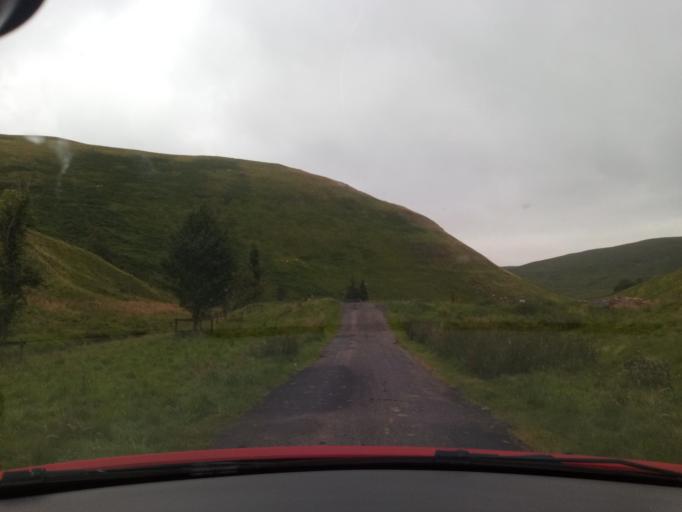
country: GB
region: England
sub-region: Northumberland
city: Rochester
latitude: 55.3975
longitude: -2.2469
